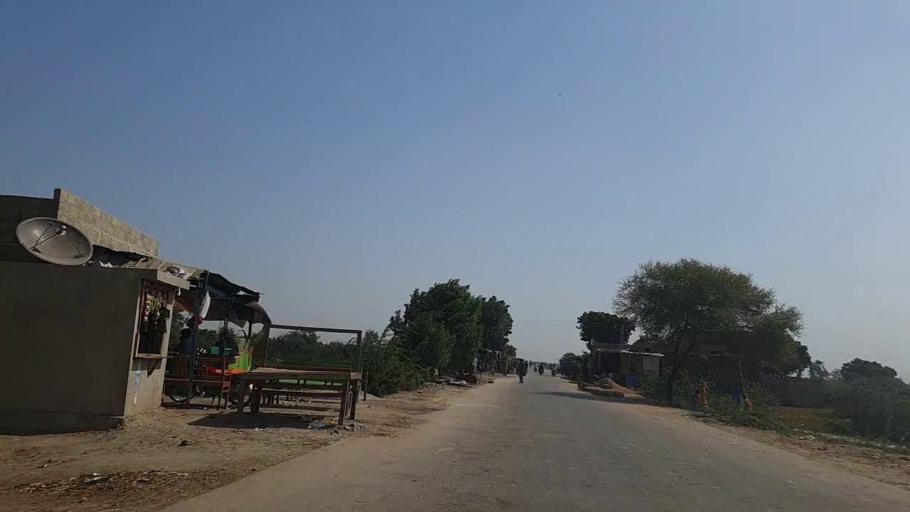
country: PK
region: Sindh
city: Mirpur Batoro
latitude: 24.7598
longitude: 68.2226
